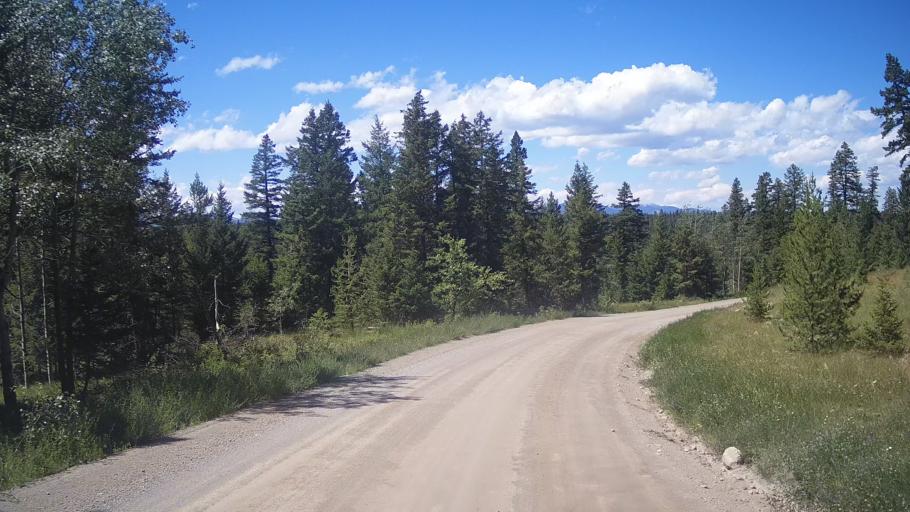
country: CA
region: British Columbia
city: Cache Creek
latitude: 51.1544
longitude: -121.5468
